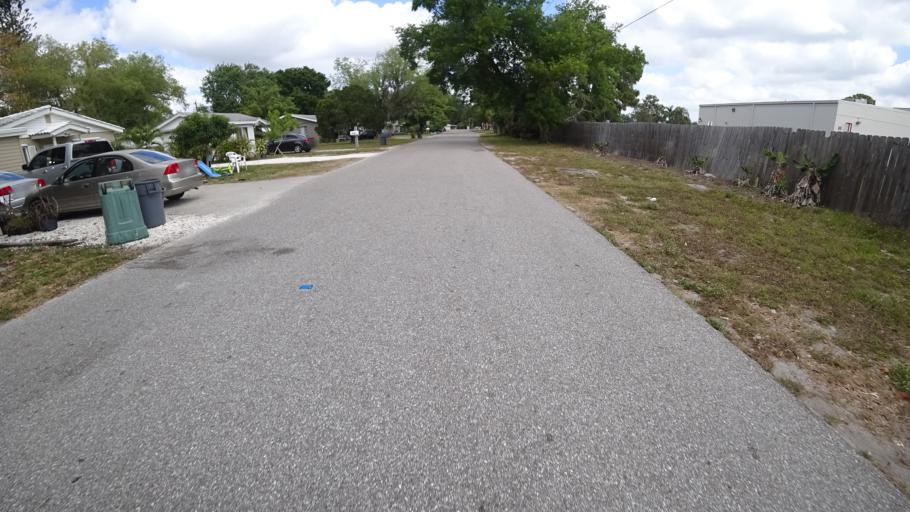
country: US
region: Florida
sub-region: Manatee County
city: Bayshore Gardens
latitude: 27.4385
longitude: -82.5775
